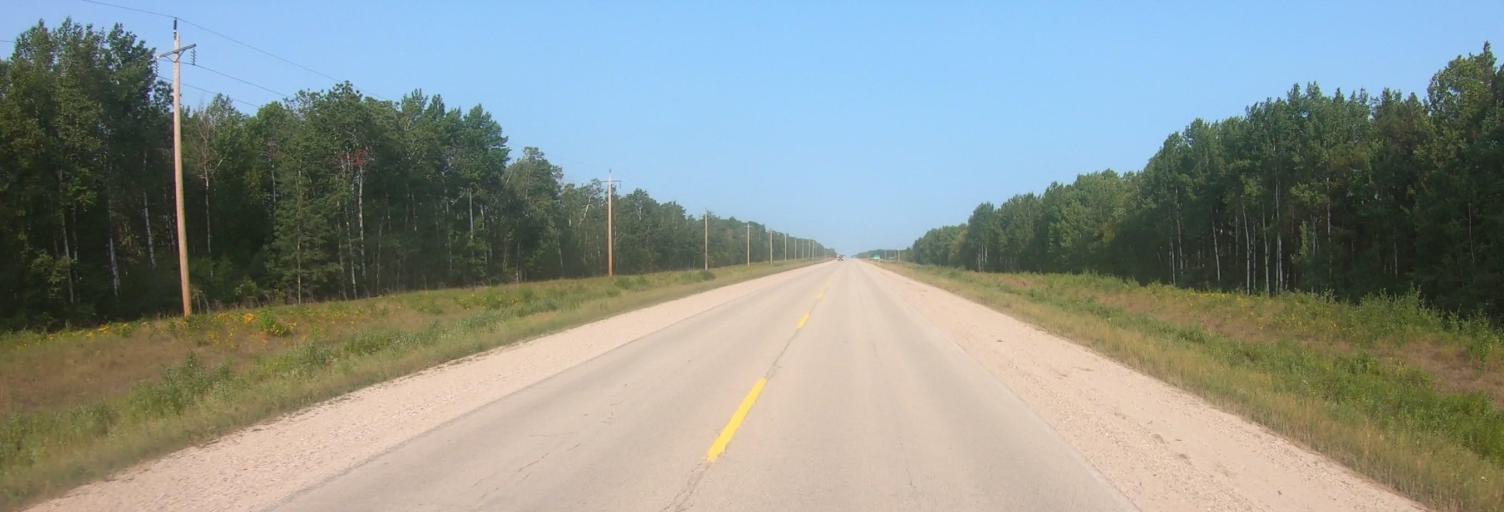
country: US
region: Minnesota
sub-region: Roseau County
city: Roseau
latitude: 49.0281
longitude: -95.7483
